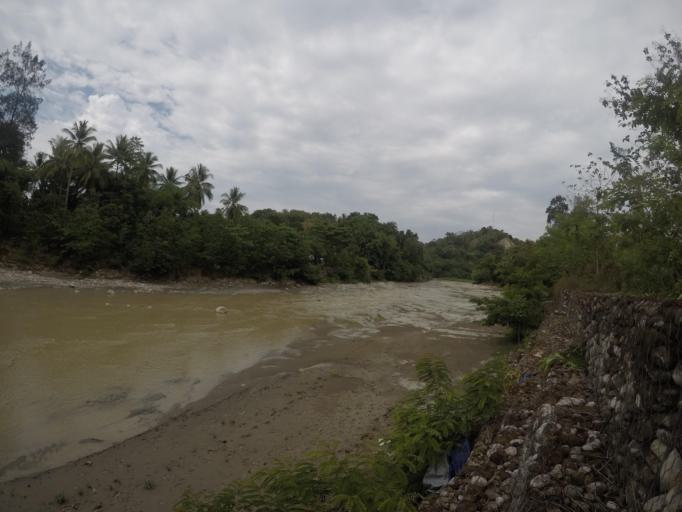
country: TL
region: Viqueque
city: Viqueque
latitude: -8.8649
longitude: 126.3657
